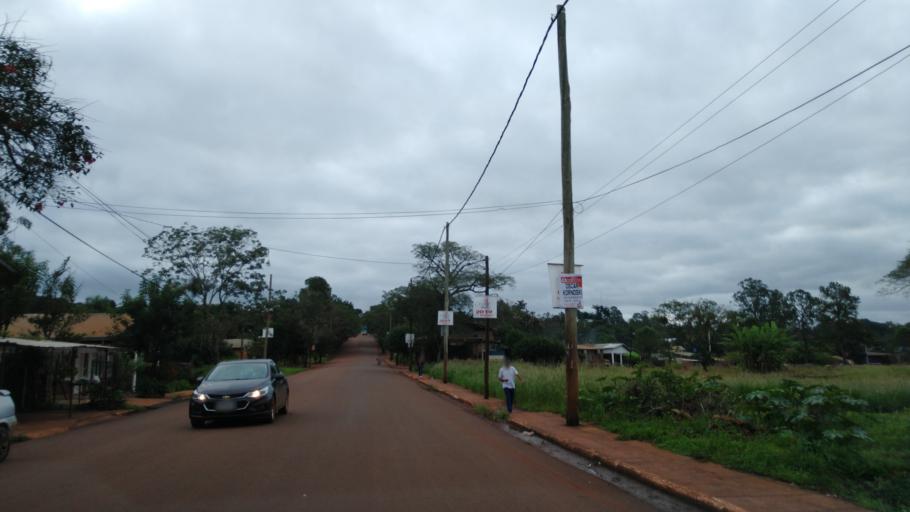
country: AR
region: Misiones
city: Jardin America
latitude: -27.0381
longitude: -55.2327
